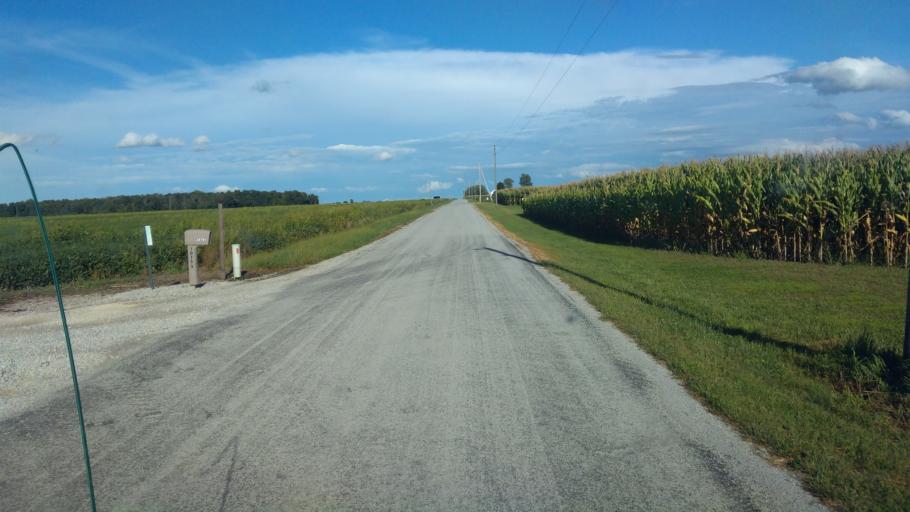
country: US
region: Ohio
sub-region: Hardin County
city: Kenton
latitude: 40.7614
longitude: -83.6762
